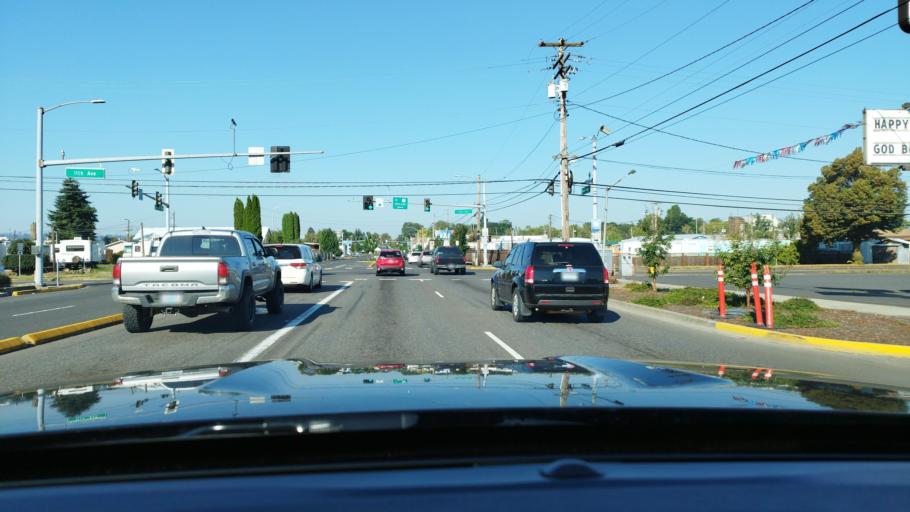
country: US
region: Washington
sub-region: Cowlitz County
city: Longview
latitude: 46.1255
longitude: -122.9364
